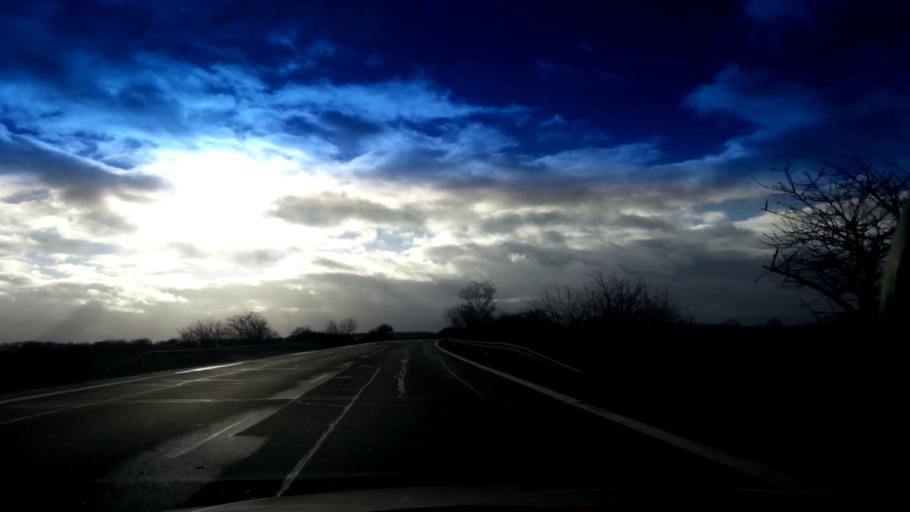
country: CZ
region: Karlovarsky
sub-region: Okres Cheb
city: Frantiskovy Lazne
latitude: 50.1093
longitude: 12.3722
